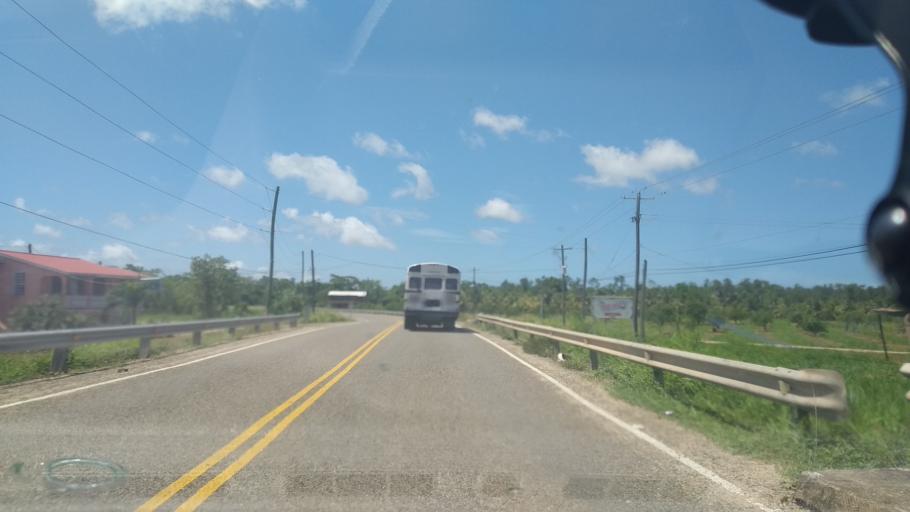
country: BZ
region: Stann Creek
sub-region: Dangriga
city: Dangriga
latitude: 16.9999
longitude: -88.3027
